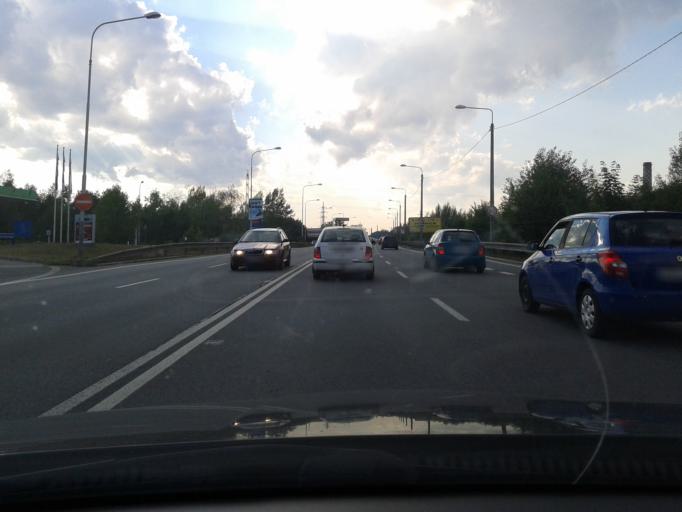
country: CZ
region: Moravskoslezsky
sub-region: Okres Ostrava-Mesto
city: Ostrava
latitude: 49.8043
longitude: 18.2882
